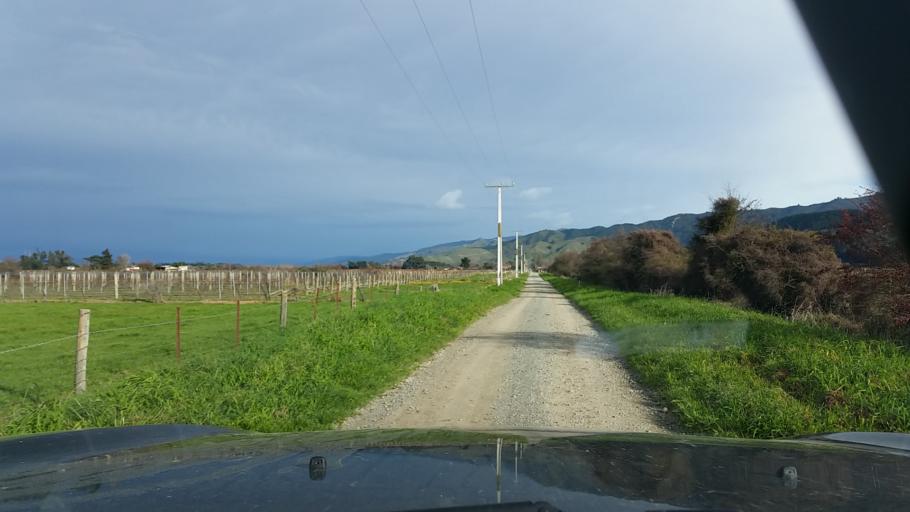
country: NZ
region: Marlborough
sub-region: Marlborough District
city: Blenheim
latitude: -41.4308
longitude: 173.9927
